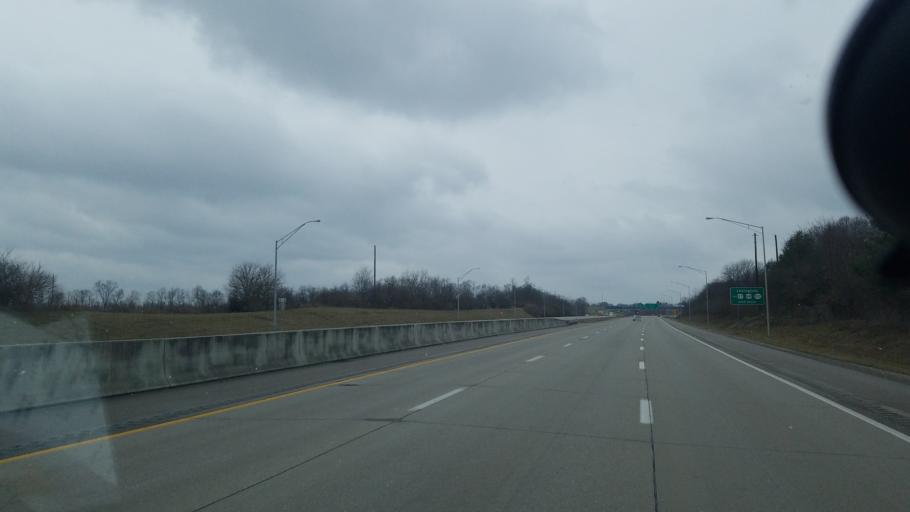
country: US
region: Kentucky
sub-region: Fayette County
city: Lexington-Fayette
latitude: 38.0581
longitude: -84.4161
